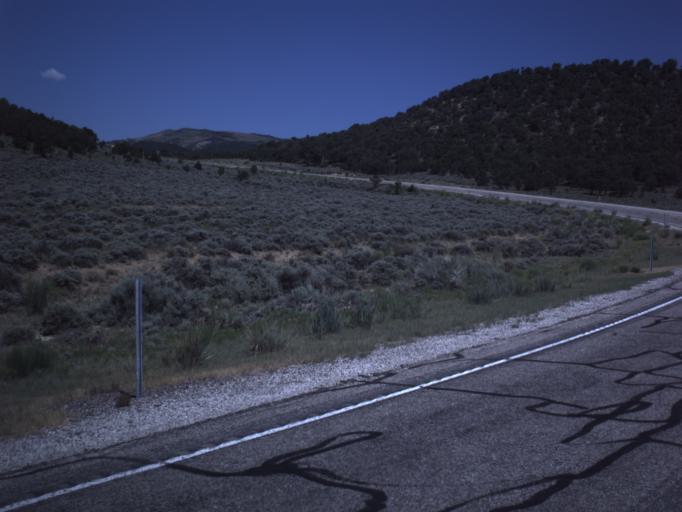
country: US
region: Utah
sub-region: Wayne County
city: Loa
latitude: 38.6439
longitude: -111.4332
